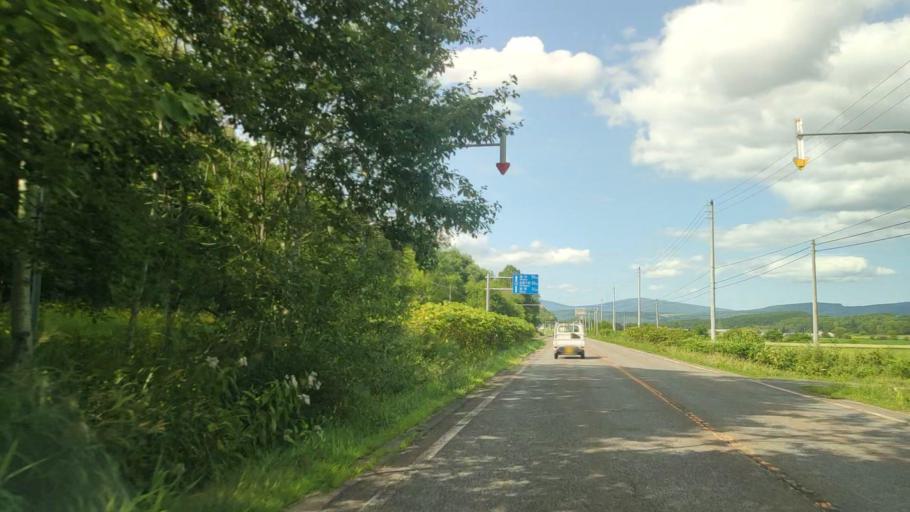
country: JP
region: Hokkaido
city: Nayoro
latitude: 44.3968
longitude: 142.3945
